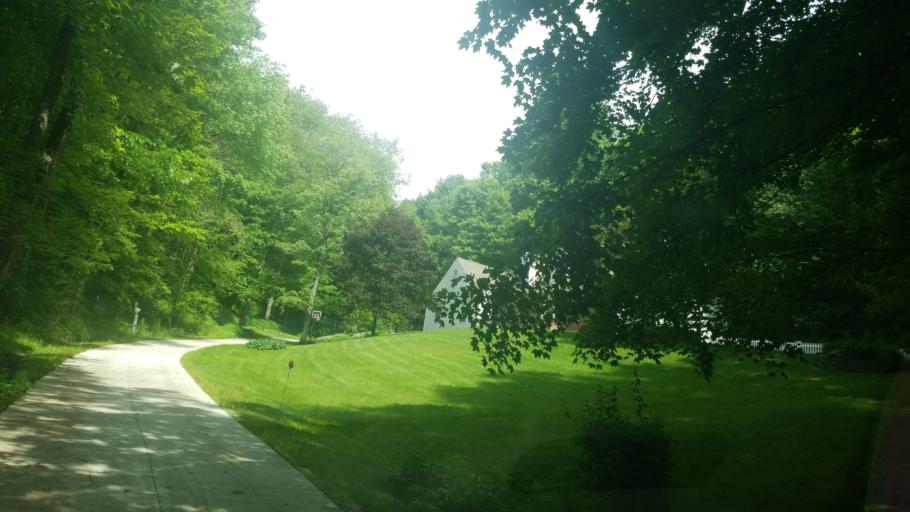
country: US
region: Ohio
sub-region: Sandusky County
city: Bellville
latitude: 40.6287
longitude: -82.5155
